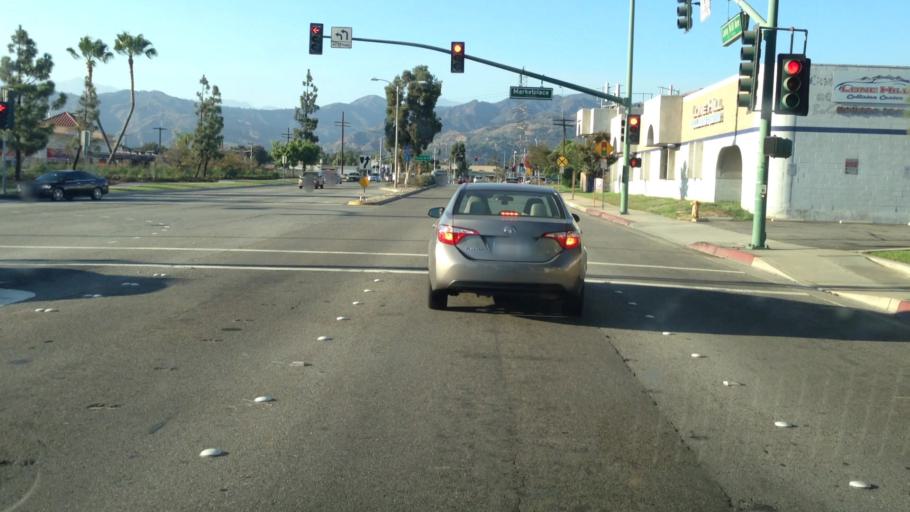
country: US
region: California
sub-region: Los Angeles County
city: Charter Oak
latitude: 34.1157
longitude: -117.8289
